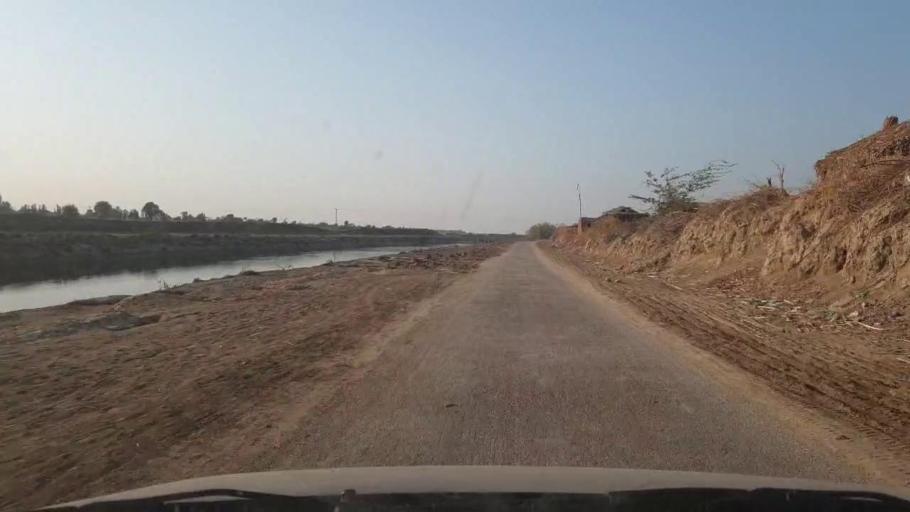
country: PK
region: Sindh
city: Samaro
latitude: 25.2872
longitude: 69.3354
